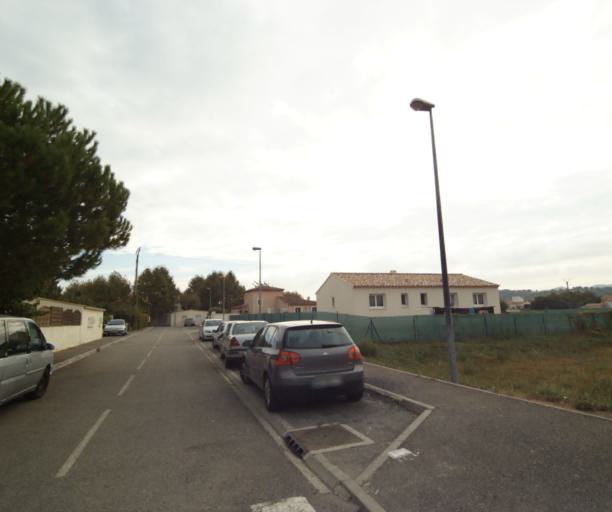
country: FR
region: Provence-Alpes-Cote d'Azur
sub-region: Departement des Bouches-du-Rhone
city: Saint-Victoret
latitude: 43.4182
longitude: 5.2516
